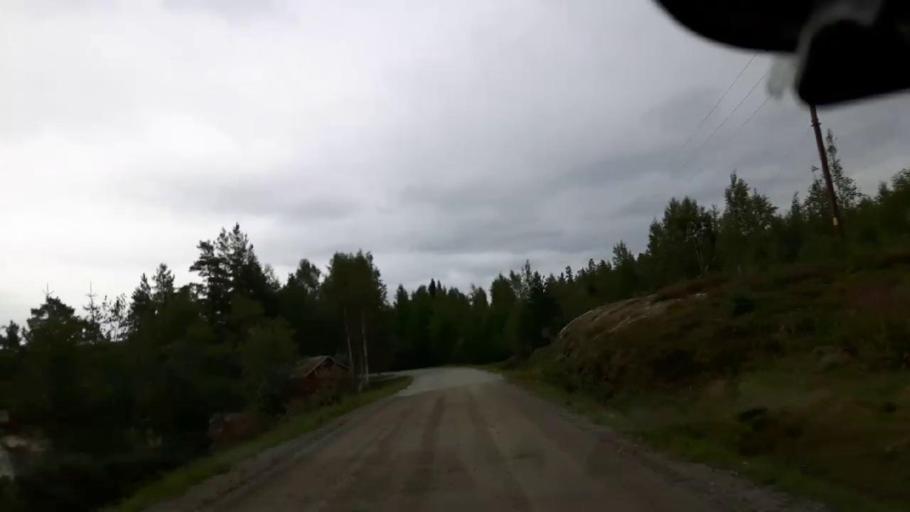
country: SE
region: Vaesternorrland
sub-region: Ange Kommun
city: Fransta
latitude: 62.7766
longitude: 16.2242
